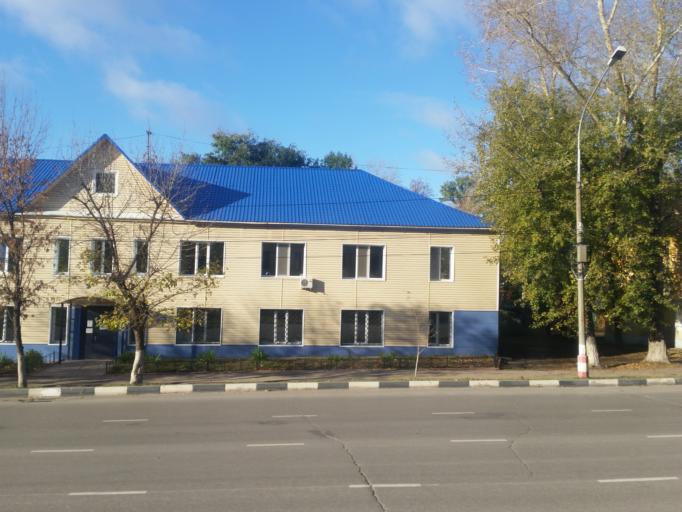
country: RU
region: Ulyanovsk
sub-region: Ulyanovskiy Rayon
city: Ulyanovsk
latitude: 54.3389
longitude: 48.3803
